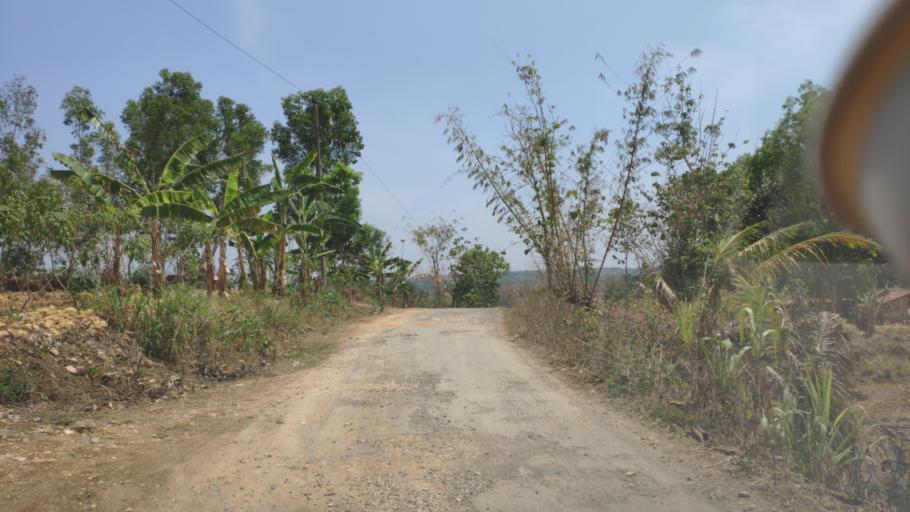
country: ID
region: Central Java
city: Guyangan
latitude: -6.9476
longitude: 111.1216
